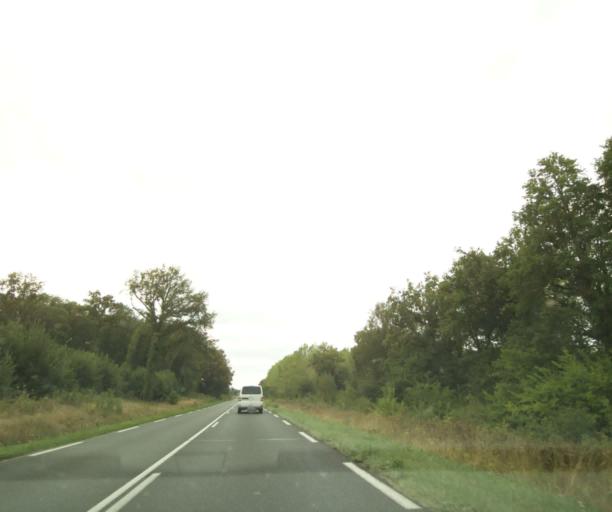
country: FR
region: Centre
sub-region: Departement d'Indre-et-Loire
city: Perrusson
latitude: 47.0733
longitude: 1.0699
